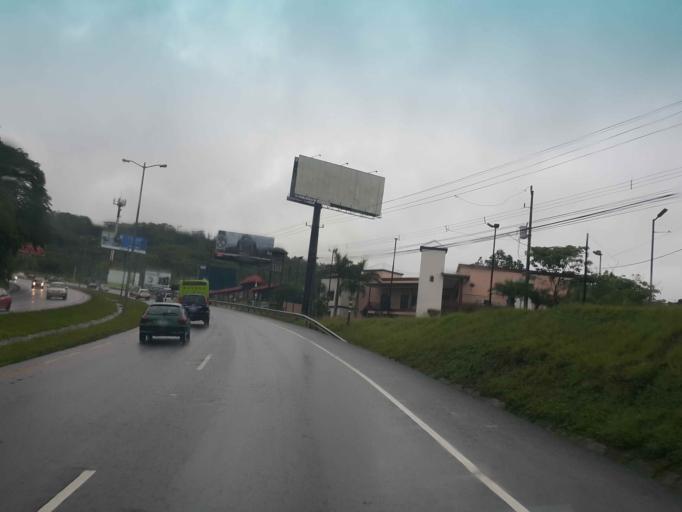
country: CR
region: San Jose
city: Santa Ana
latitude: 9.9441
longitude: -84.1723
